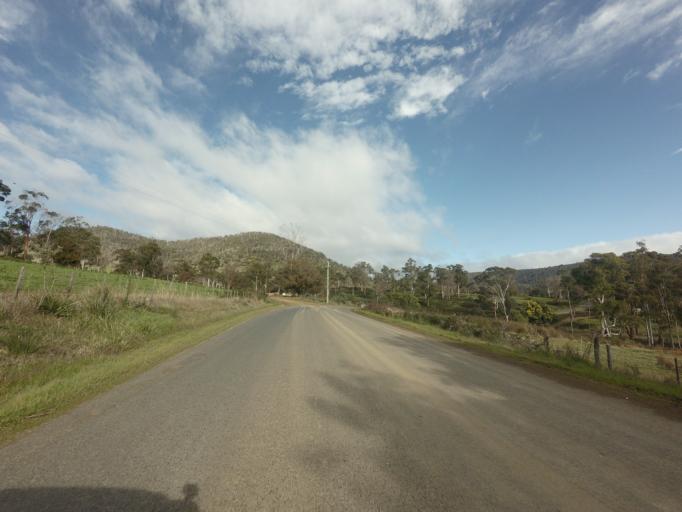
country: AU
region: Tasmania
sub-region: Derwent Valley
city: New Norfolk
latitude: -42.7767
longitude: 146.9709
